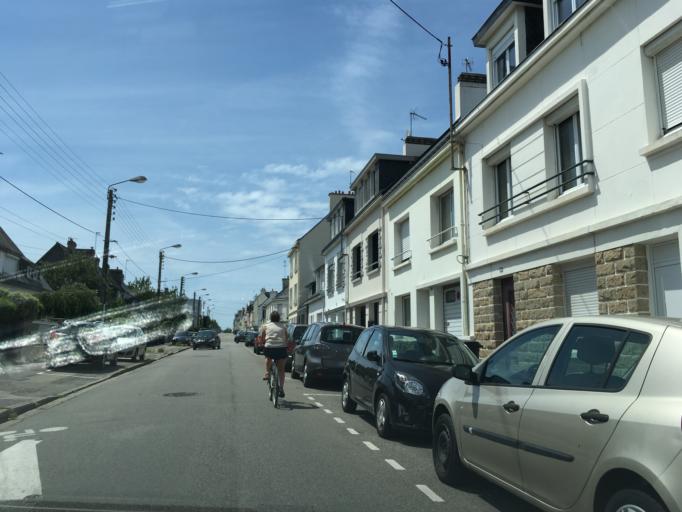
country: FR
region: Brittany
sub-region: Departement du Morbihan
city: Lorient
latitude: 47.7411
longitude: -3.3763
